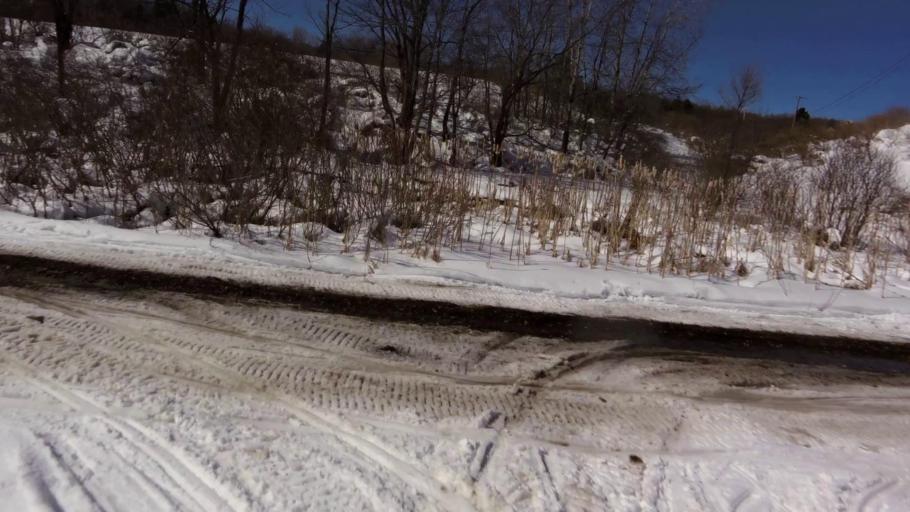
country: US
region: New York
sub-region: Wyoming County
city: Arcade
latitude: 42.4429
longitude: -78.3387
